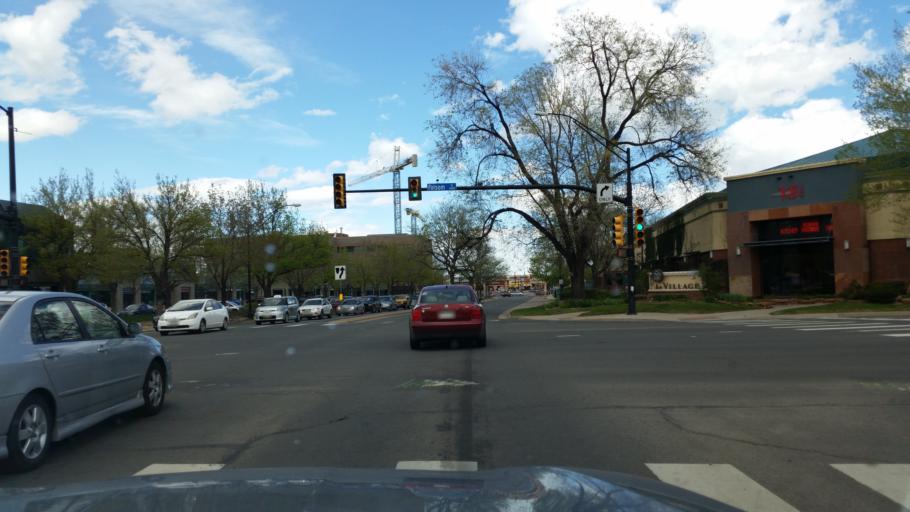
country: US
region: Colorado
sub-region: Boulder County
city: Boulder
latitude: 40.0173
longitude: -105.2634
